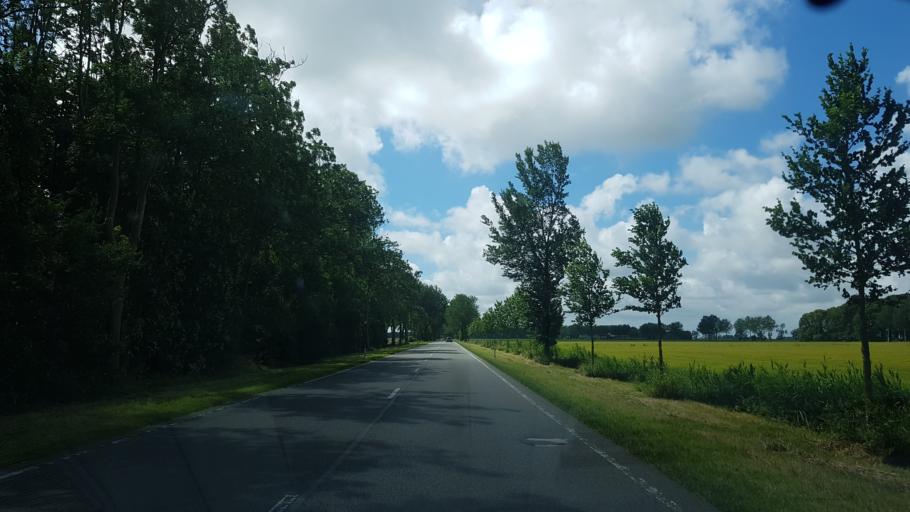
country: NL
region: Groningen
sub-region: Gemeente Bedum
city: Bedum
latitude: 53.4061
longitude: 6.6514
